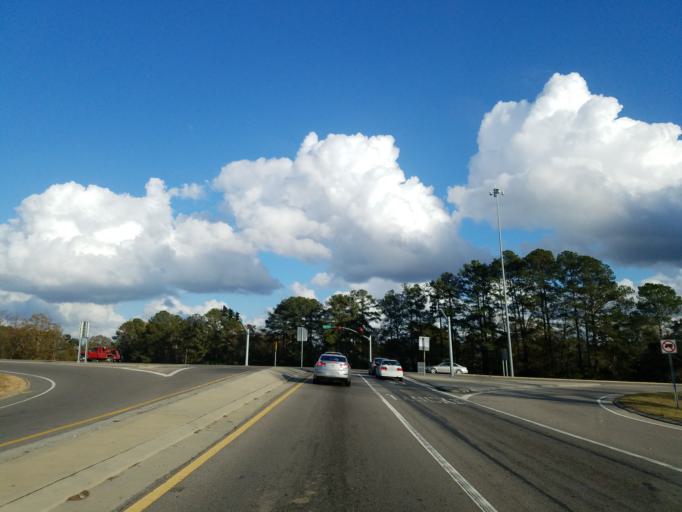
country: US
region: Mississippi
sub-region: Jones County
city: Laurel
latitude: 31.6830
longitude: -89.1474
